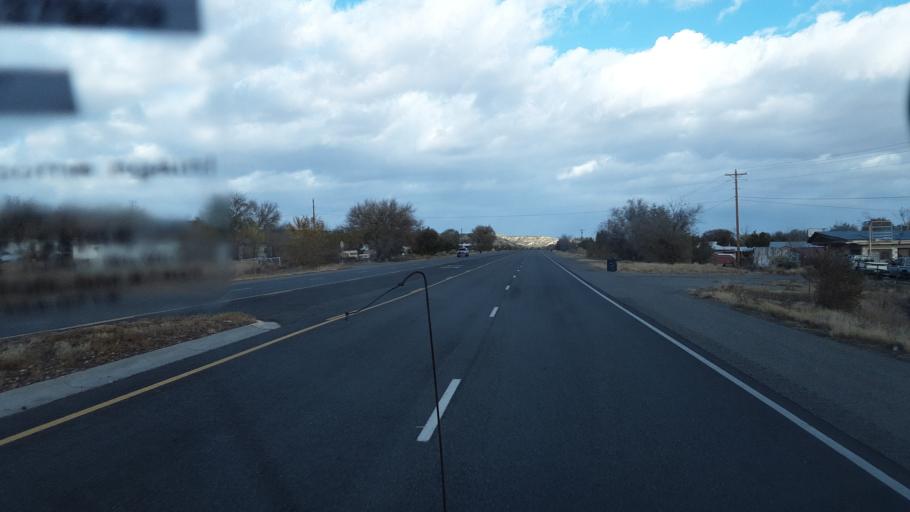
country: US
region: New Mexico
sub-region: Rio Arriba County
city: Ohkay Owingeh
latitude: 36.0416
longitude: -106.1019
